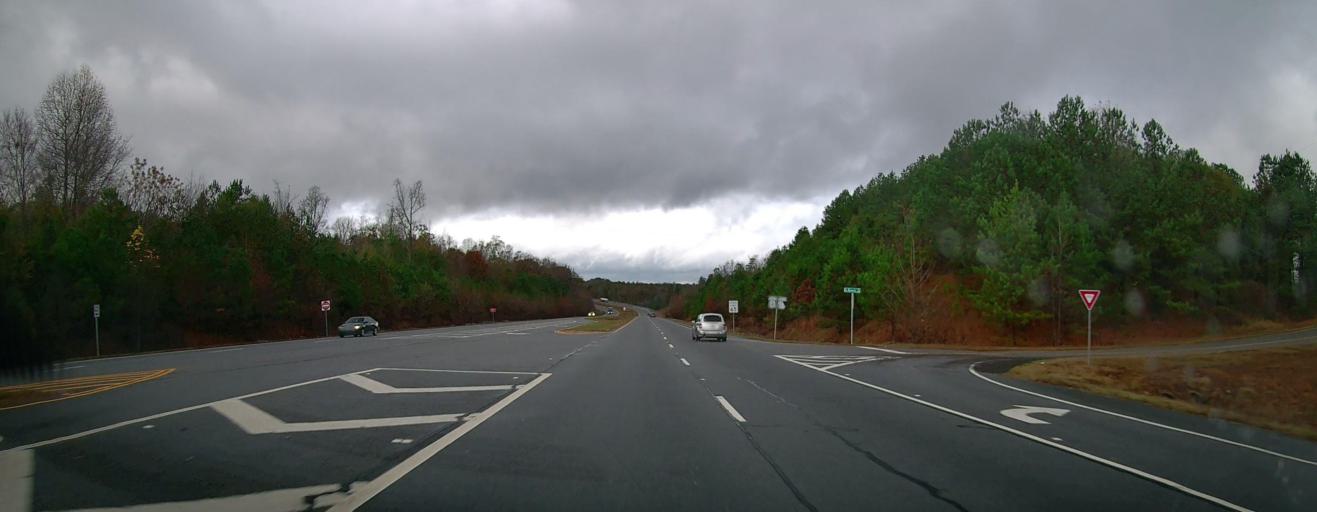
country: US
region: Georgia
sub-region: Clarke County
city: Country Club Estates
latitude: 34.0537
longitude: -83.4089
